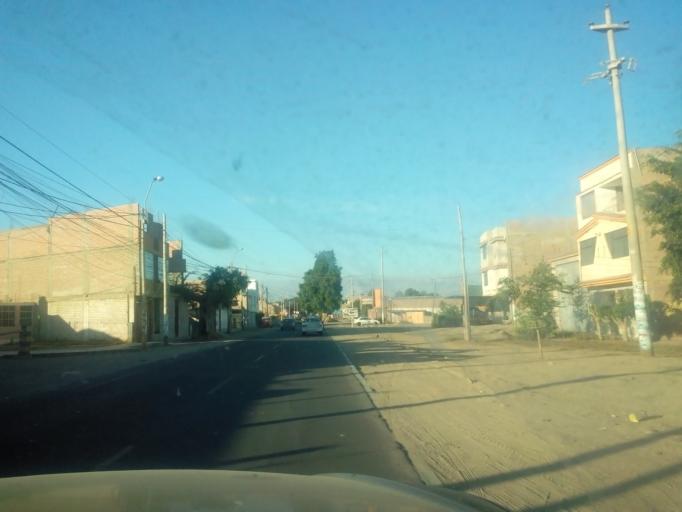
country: PE
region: Ica
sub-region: Provincia de Ica
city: Ica
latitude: -14.0795
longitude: -75.7471
